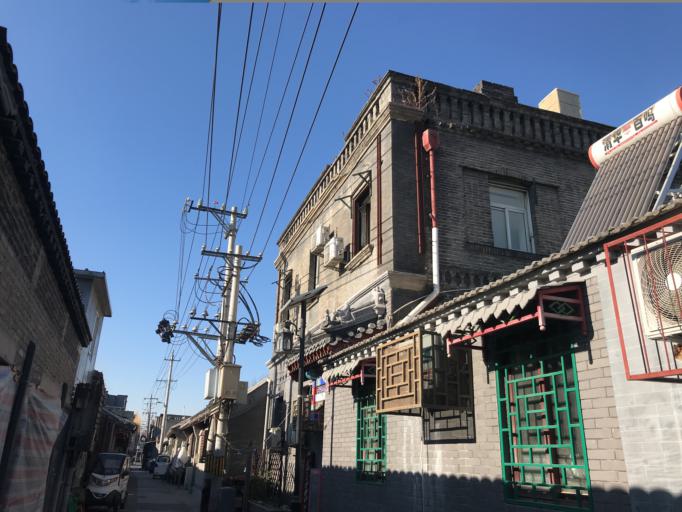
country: CN
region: Beijing
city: Beijing
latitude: 39.8917
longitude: 116.3896
